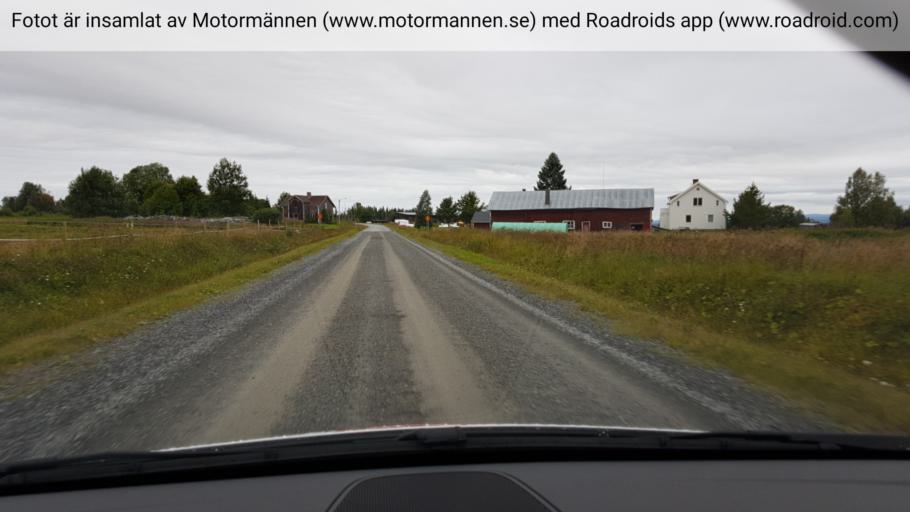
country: SE
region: Jaemtland
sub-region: OEstersunds Kommun
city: Lit
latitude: 63.6811
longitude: 14.8577
